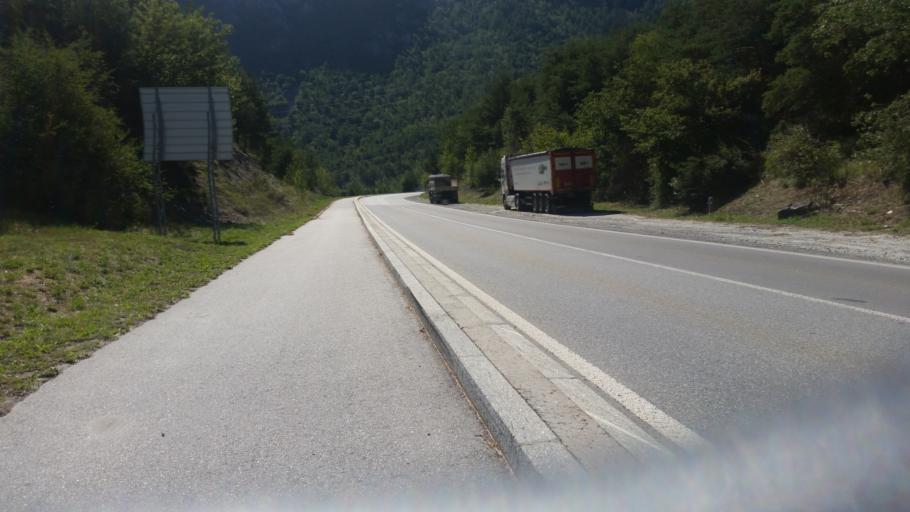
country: CH
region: Valais
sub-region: Sierre District
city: Chippis
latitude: 46.2924
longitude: 7.5589
